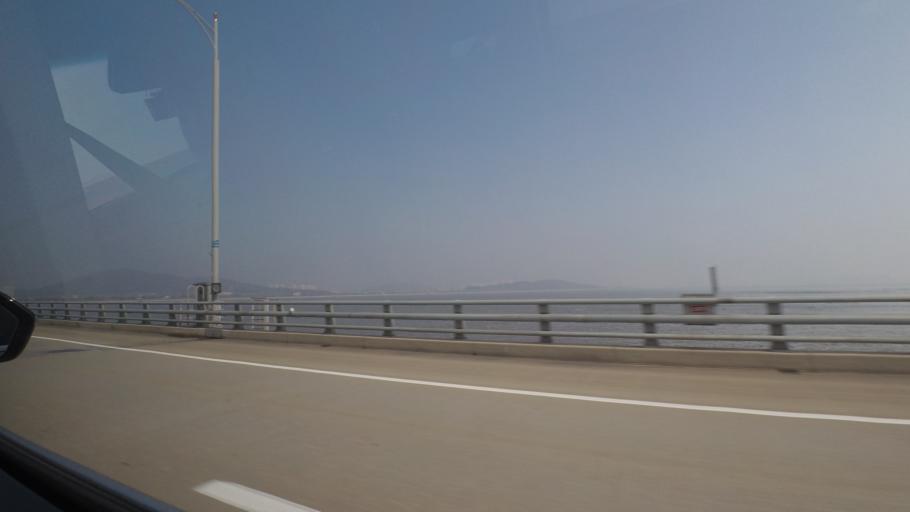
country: KR
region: Incheon
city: Incheon
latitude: 37.4560
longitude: 126.5240
